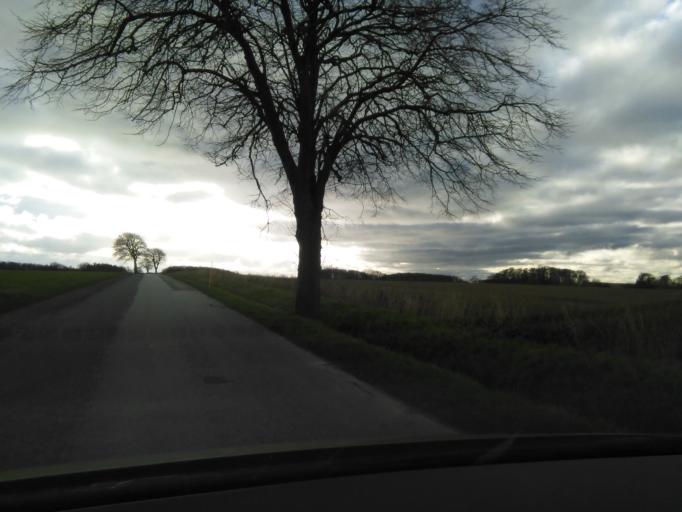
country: DK
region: Central Jutland
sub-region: Odder Kommune
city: Odder
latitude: 55.8782
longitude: 10.1704
